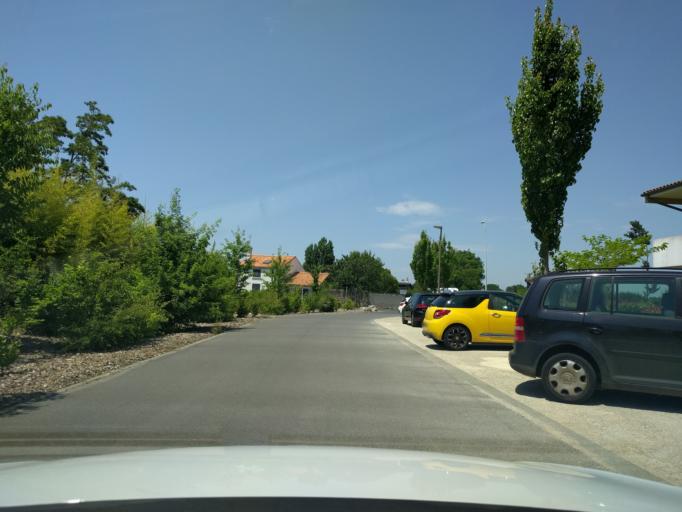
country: FR
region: Poitou-Charentes
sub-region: Departement des Deux-Sevres
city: Niort
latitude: 46.3461
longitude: -0.4601
